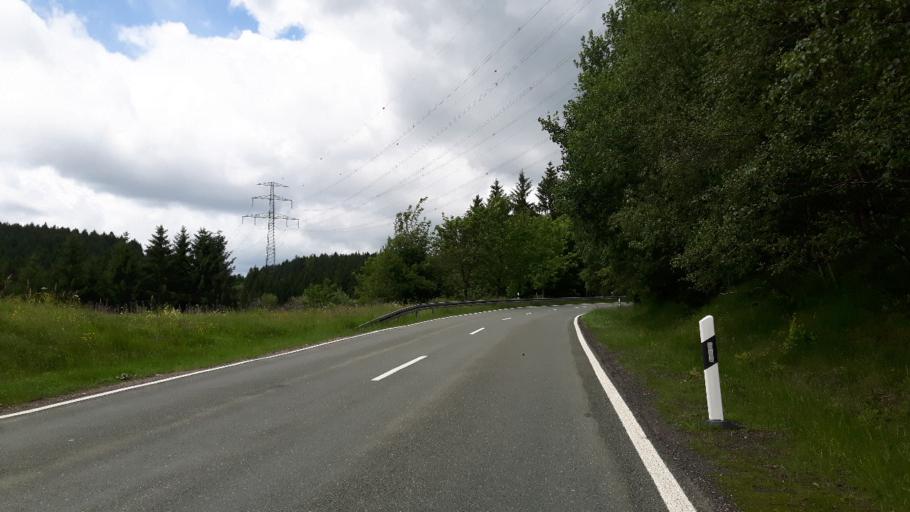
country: DE
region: Thuringia
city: Grossbreitenbach
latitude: 50.5755
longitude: 11.0121
